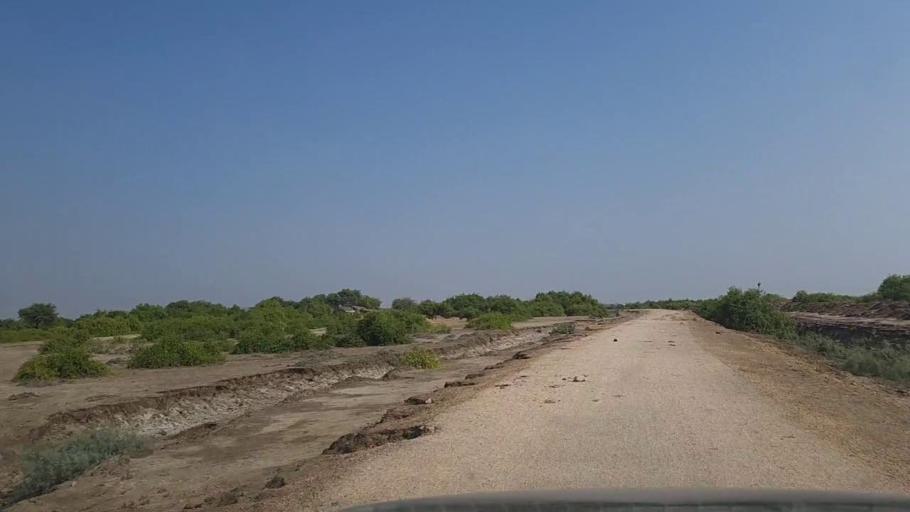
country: PK
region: Sindh
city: Mirpur Sakro
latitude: 24.5031
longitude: 67.7783
